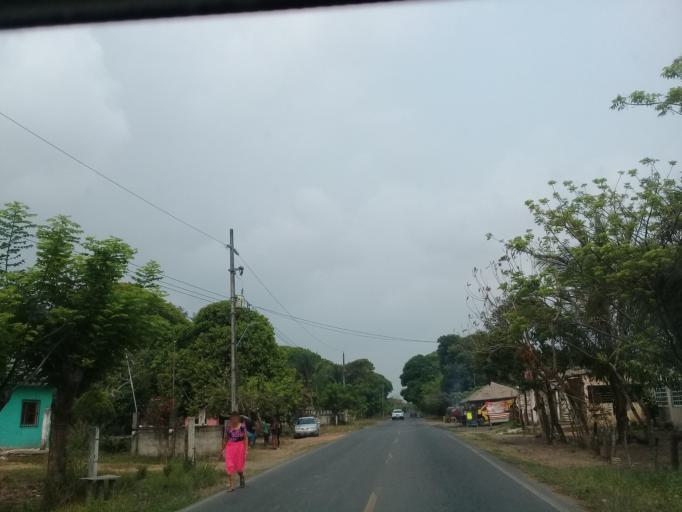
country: MX
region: Veracruz
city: El Tejar
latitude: 19.0547
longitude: -96.1928
